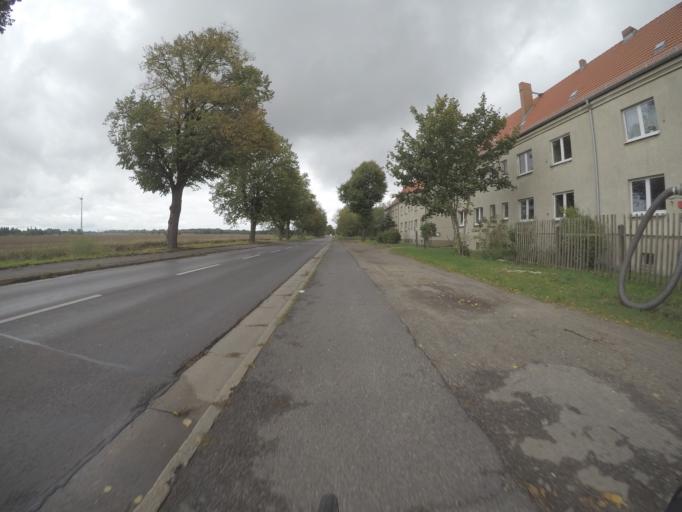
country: DE
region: Berlin
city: Buchholz
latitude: 52.6194
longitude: 13.4508
